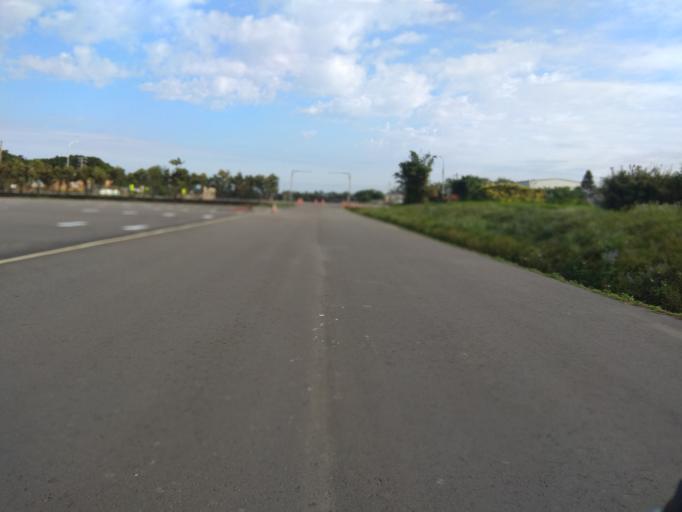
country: TW
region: Taiwan
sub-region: Hsinchu
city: Zhubei
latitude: 25.0063
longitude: 121.0450
